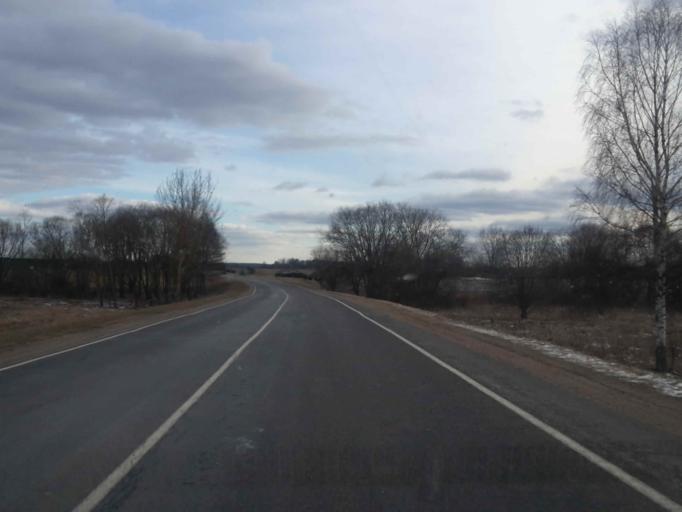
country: BY
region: Minsk
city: Kryvichy
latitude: 54.6835
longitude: 27.1517
